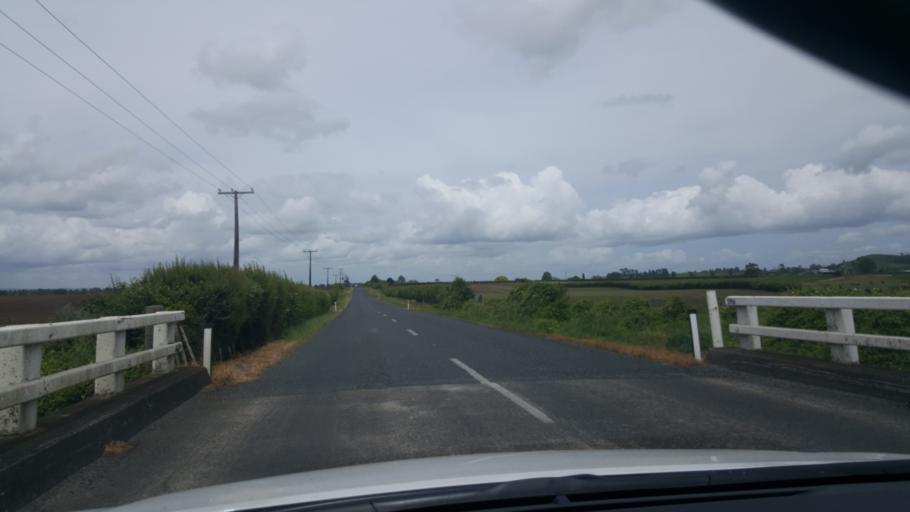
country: NZ
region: Waikato
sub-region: Matamata-Piako District
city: Matamata
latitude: -37.8758
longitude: 175.7265
